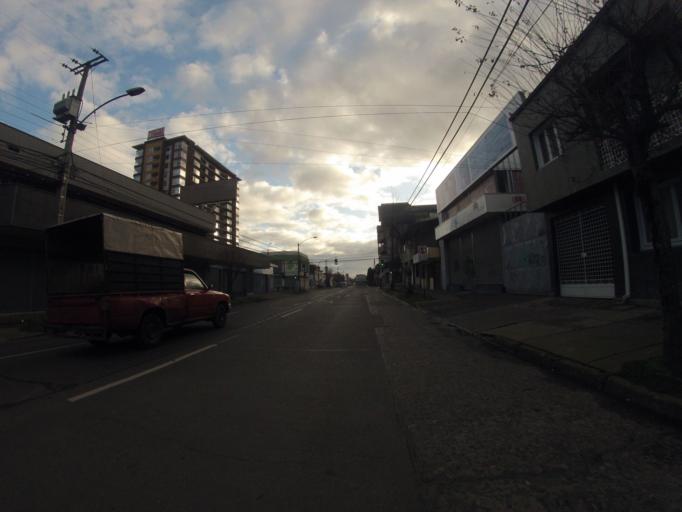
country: CL
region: Araucania
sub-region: Provincia de Cautin
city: Temuco
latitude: -38.7420
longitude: -72.5949
